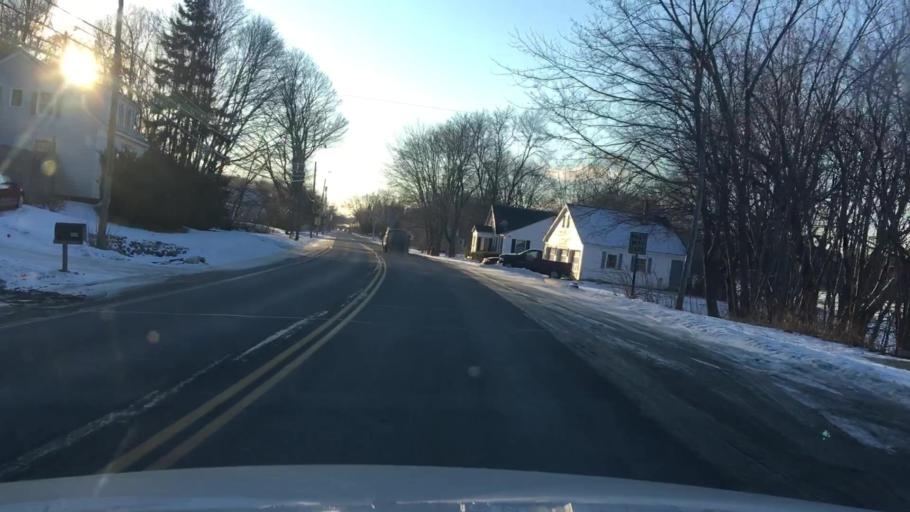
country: US
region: Maine
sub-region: Penobscot County
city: Veazie
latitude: 44.8194
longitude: -68.7169
